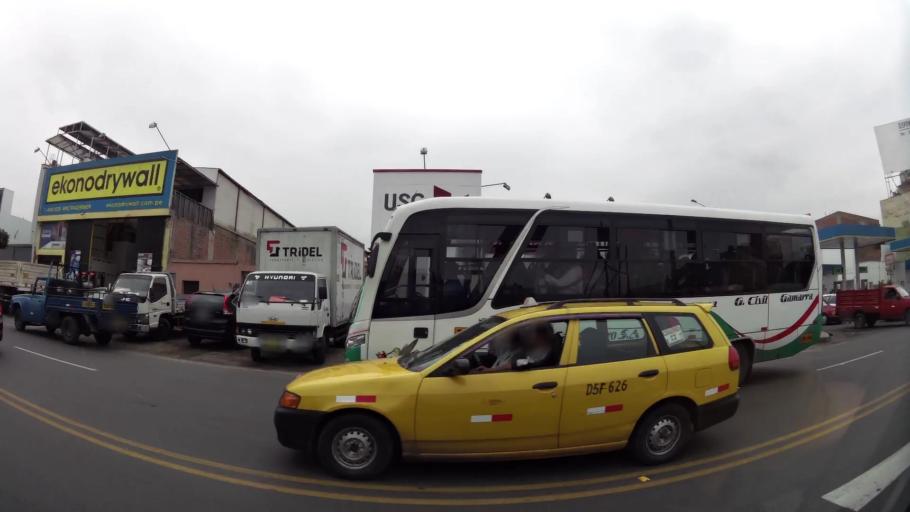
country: PE
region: Lima
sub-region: Lima
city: Surco
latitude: -12.1147
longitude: -77.0181
